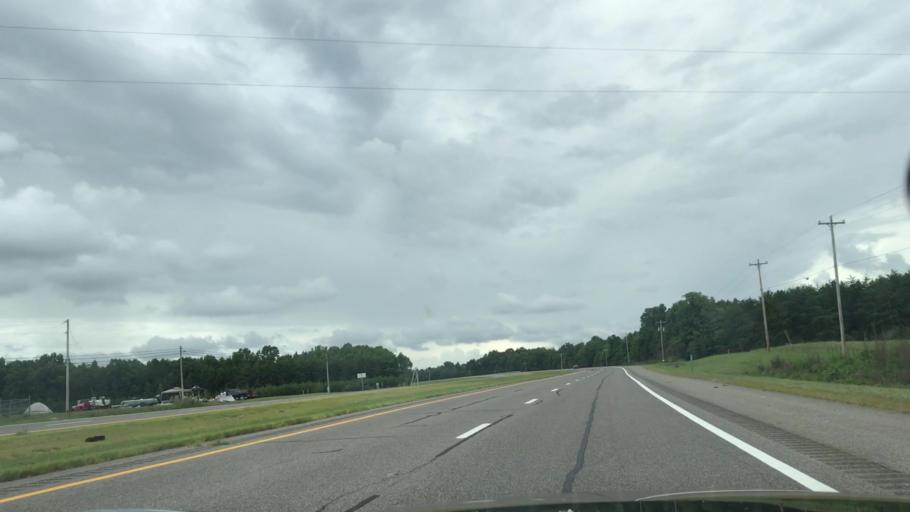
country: US
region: Tennessee
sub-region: Fentress County
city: Jamestown
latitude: 36.3535
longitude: -84.9507
